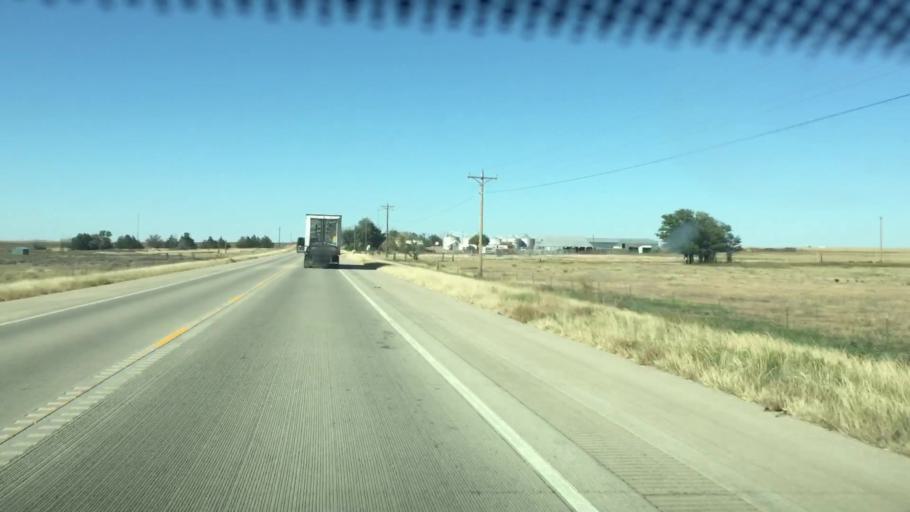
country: US
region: Colorado
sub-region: Kiowa County
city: Eads
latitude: 38.4606
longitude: -102.7307
